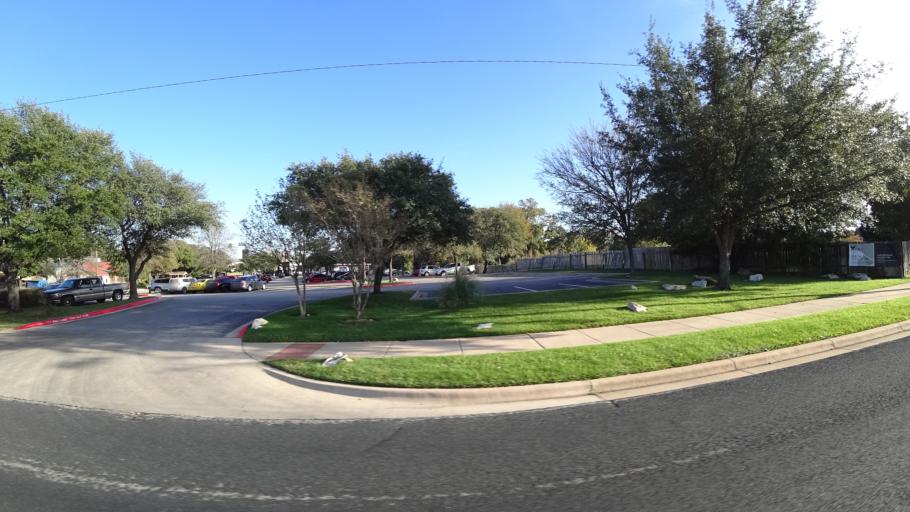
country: US
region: Texas
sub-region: Williamson County
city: Jollyville
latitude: 30.4185
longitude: -97.7490
